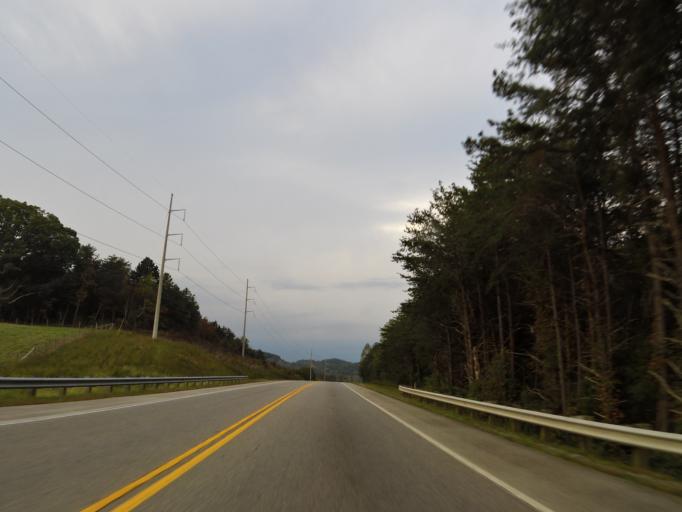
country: US
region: Tennessee
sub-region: Monroe County
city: Vonore
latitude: 35.6174
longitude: -84.2742
